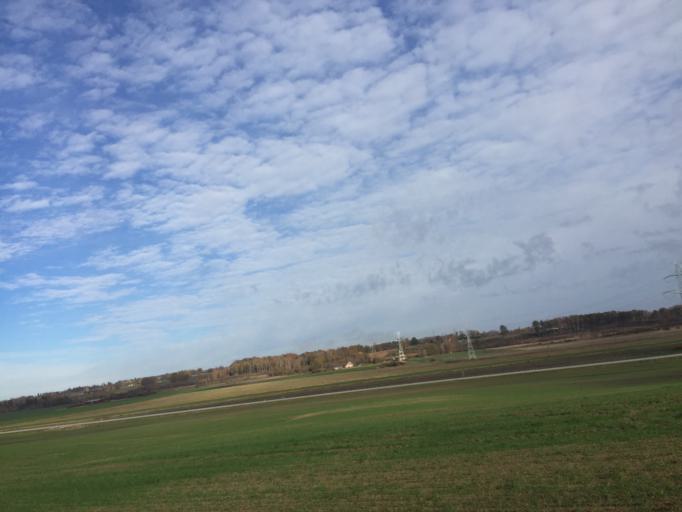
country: LV
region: Tukuma Rajons
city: Tukums
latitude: 56.9582
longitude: 23.0735
